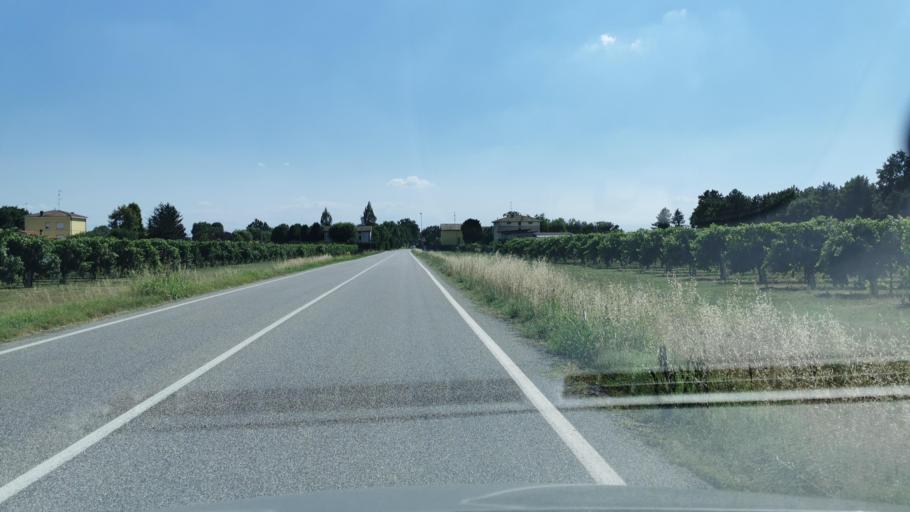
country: IT
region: Emilia-Romagna
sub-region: Provincia di Modena
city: Sam Marino
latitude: 44.7951
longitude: 10.9132
